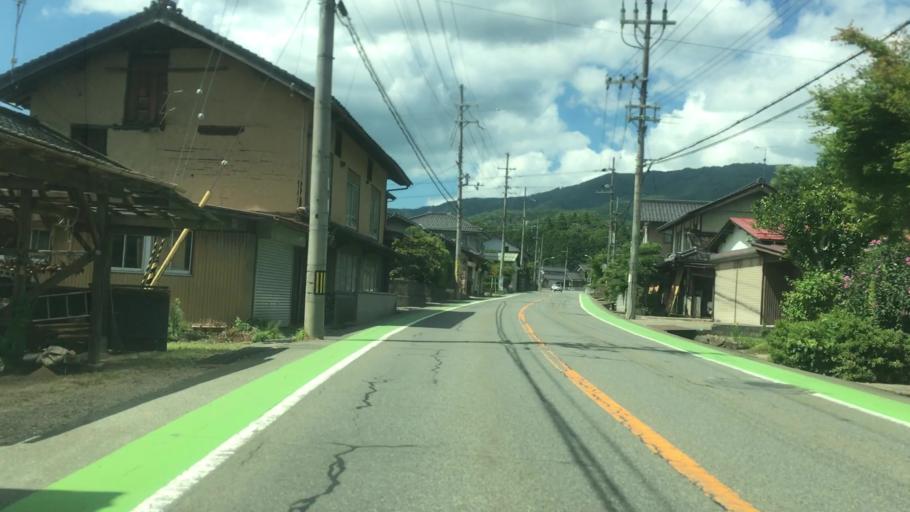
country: JP
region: Hyogo
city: Toyooka
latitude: 35.4787
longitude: 134.7087
